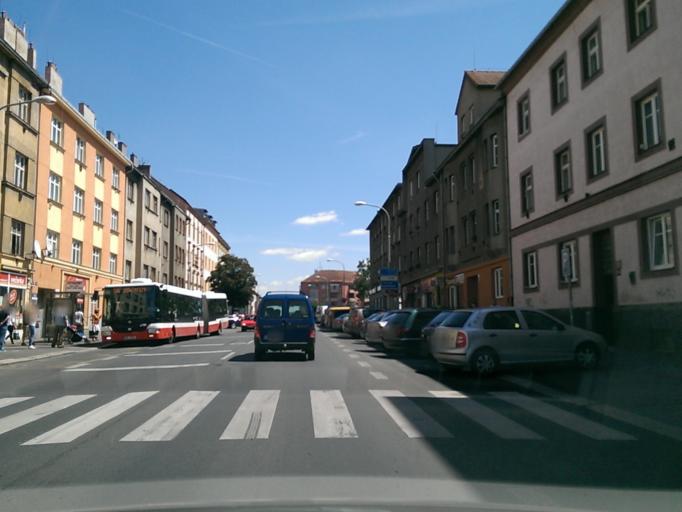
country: CZ
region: Praha
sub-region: Praha 8
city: Liben
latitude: 50.1004
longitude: 14.4883
